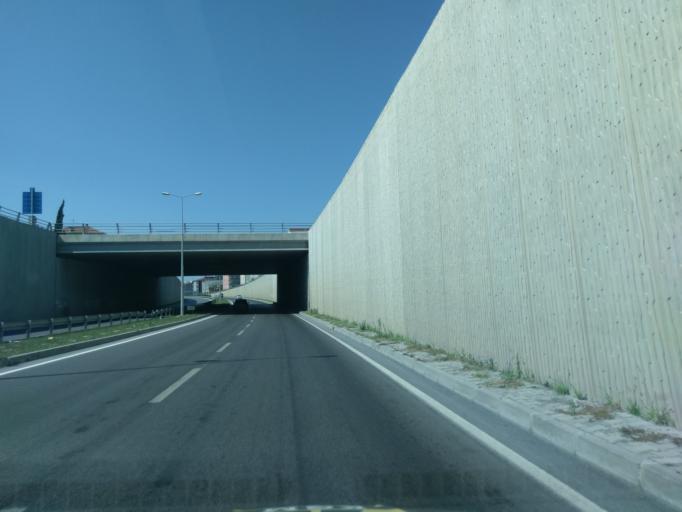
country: TR
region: Samsun
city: Bafra
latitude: 41.5517
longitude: 35.9252
